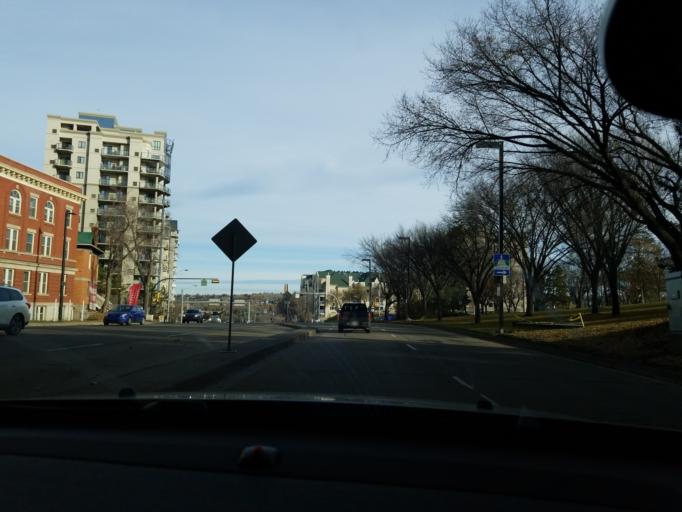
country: CA
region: Alberta
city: Edmonton
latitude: 53.5342
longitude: -113.5042
